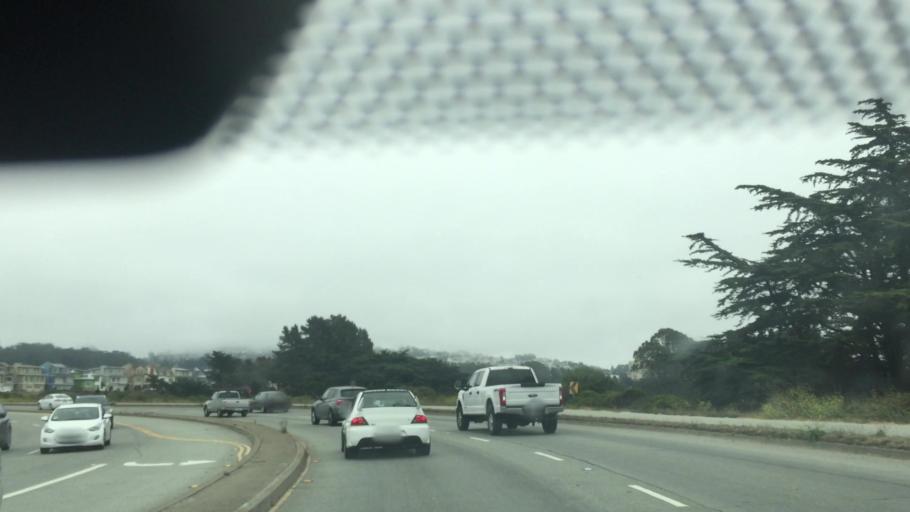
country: US
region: California
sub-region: San Mateo County
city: Daly City
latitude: 37.7289
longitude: -122.4918
